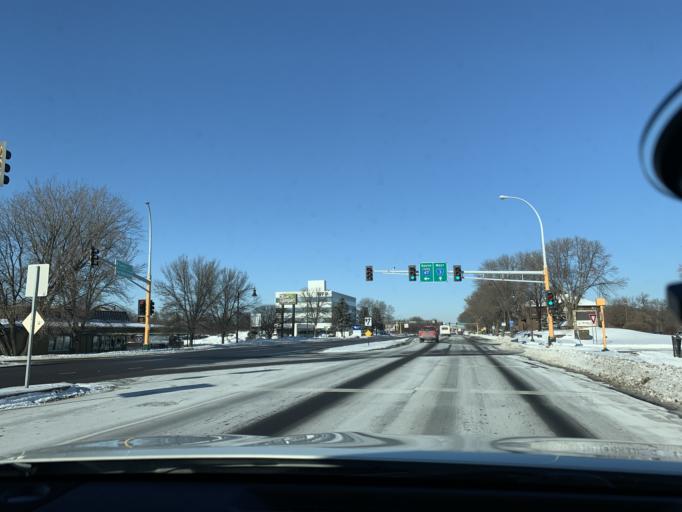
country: US
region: Minnesota
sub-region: Anoka County
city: Coon Rapids
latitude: 45.1364
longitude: -93.2709
